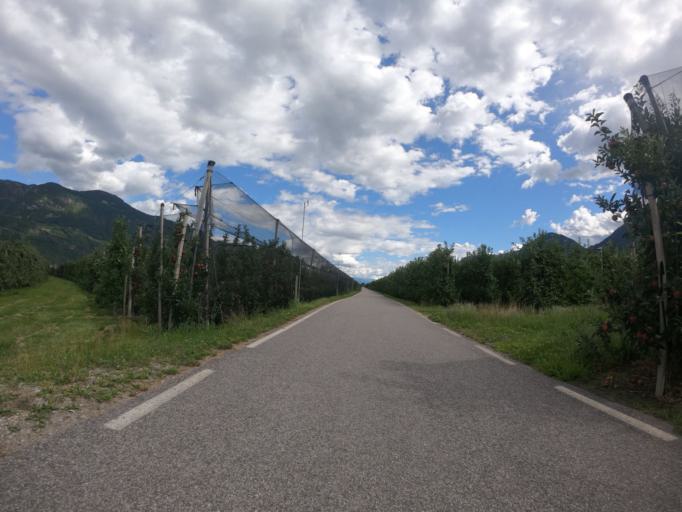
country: IT
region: Trentino-Alto Adige
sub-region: Bolzano
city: Cermes
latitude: 46.6295
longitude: 11.1529
